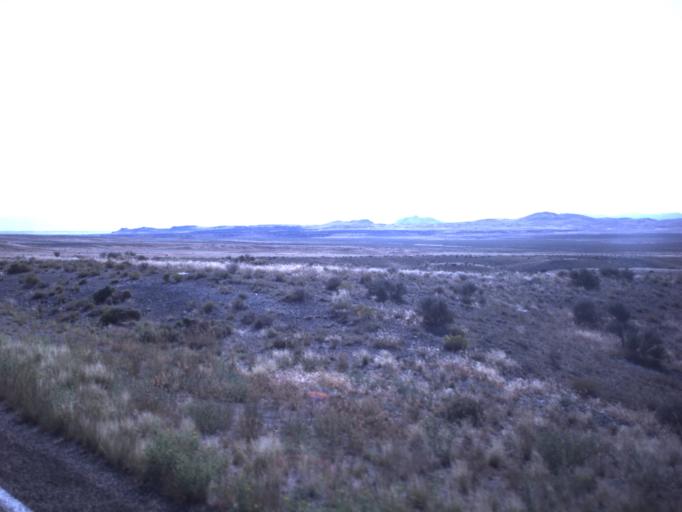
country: US
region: Utah
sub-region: Beaver County
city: Milford
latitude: 38.7866
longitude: -112.9177
